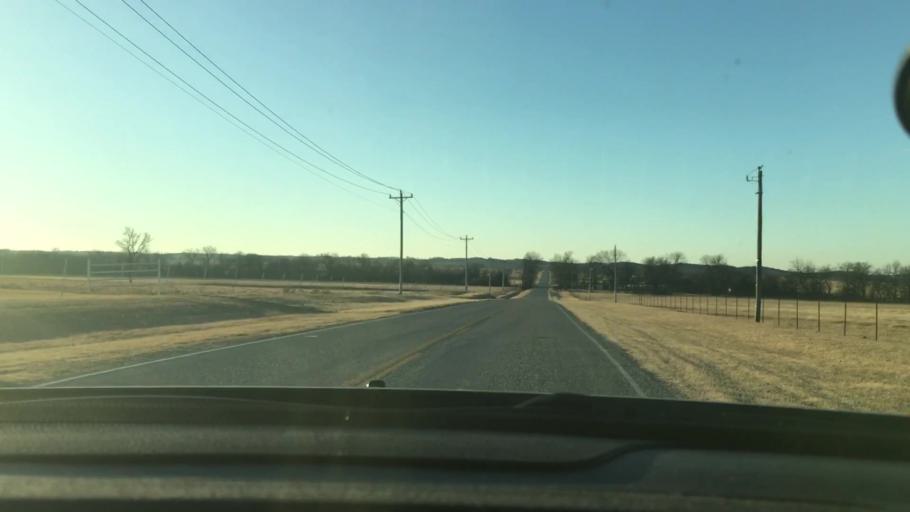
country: US
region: Oklahoma
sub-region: Murray County
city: Davis
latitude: 34.4876
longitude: -97.0906
